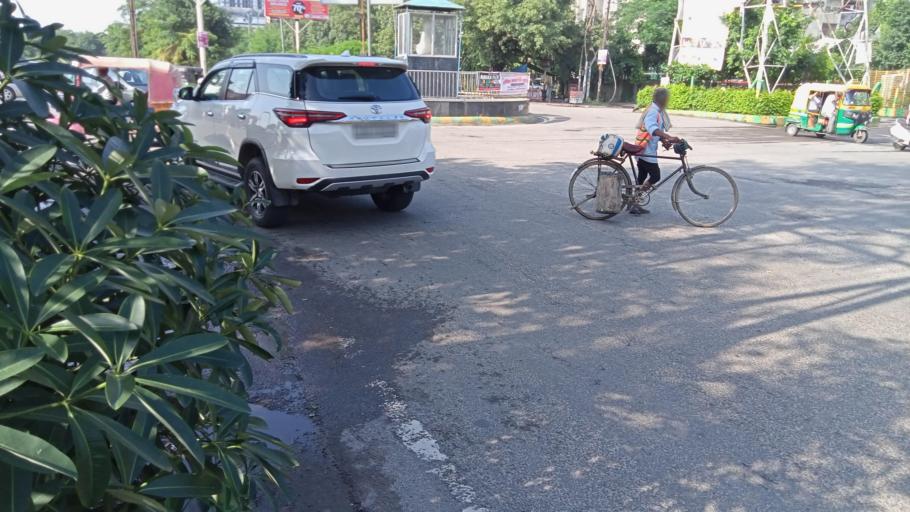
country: IN
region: Uttar Pradesh
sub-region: Ghaziabad
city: Ghaziabad
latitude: 28.6622
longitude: 77.3735
